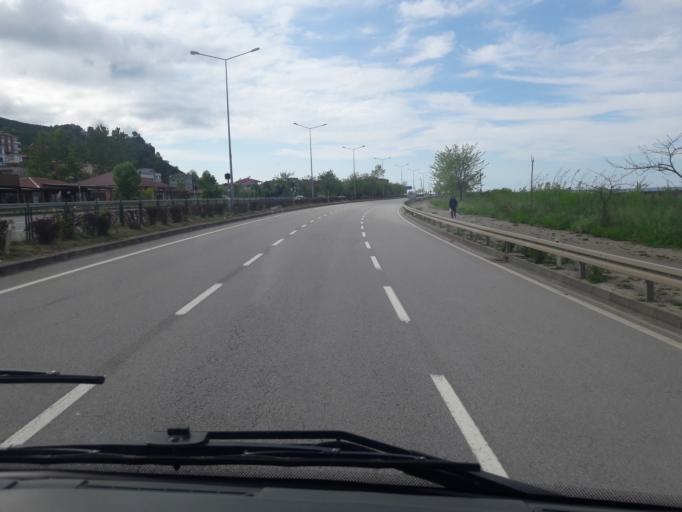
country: TR
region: Giresun
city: Piraziz
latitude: 40.9544
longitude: 38.1216
